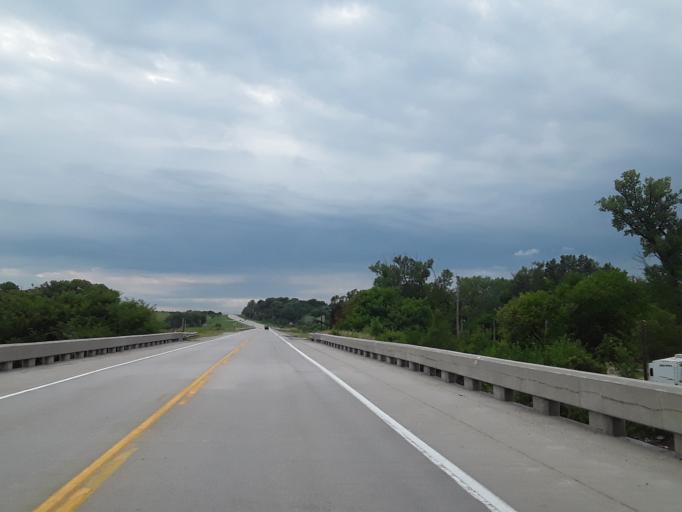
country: US
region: Nebraska
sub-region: Saunders County
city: Yutan
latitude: 41.2343
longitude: -96.3595
